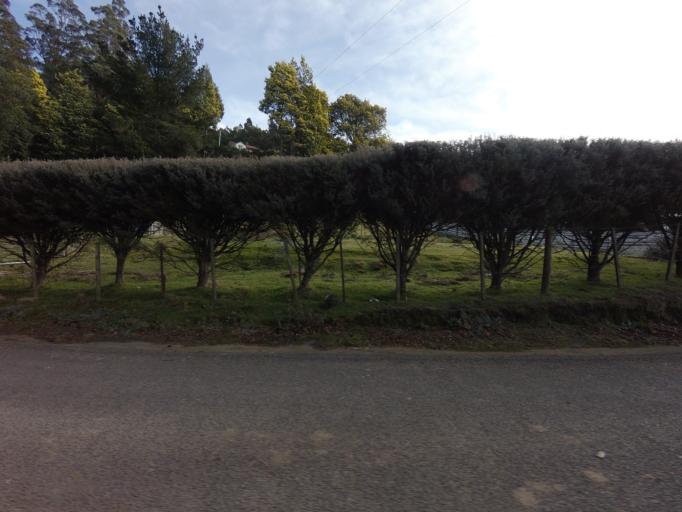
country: AU
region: Tasmania
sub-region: Kingborough
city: Margate
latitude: -43.0209
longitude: 147.1638
